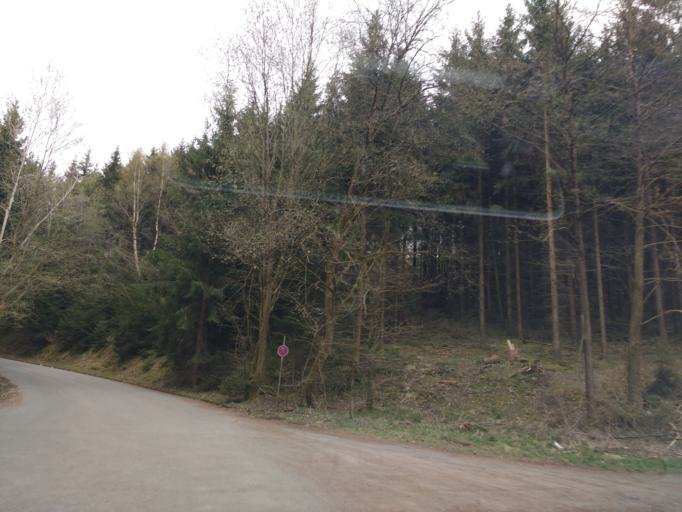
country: DE
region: North Rhine-Westphalia
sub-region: Regierungsbezirk Detmold
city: Wunnenberg
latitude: 51.4959
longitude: 8.7138
